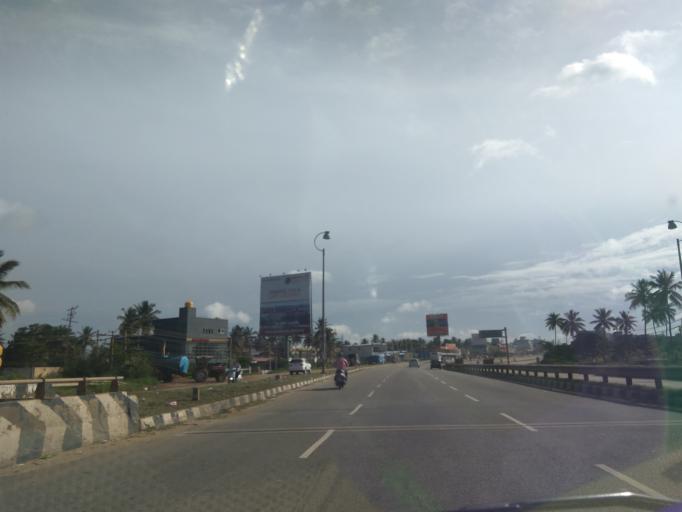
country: IN
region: Karnataka
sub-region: Bangalore Rural
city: Hoskote
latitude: 13.0655
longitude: 77.7761
